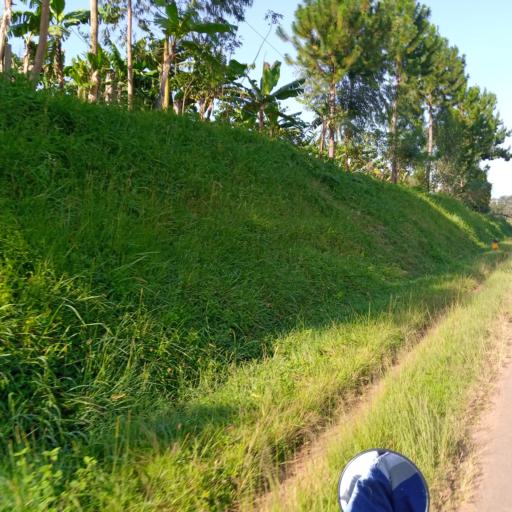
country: UG
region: Central Region
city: Masaka
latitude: -0.4181
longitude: 31.6753
